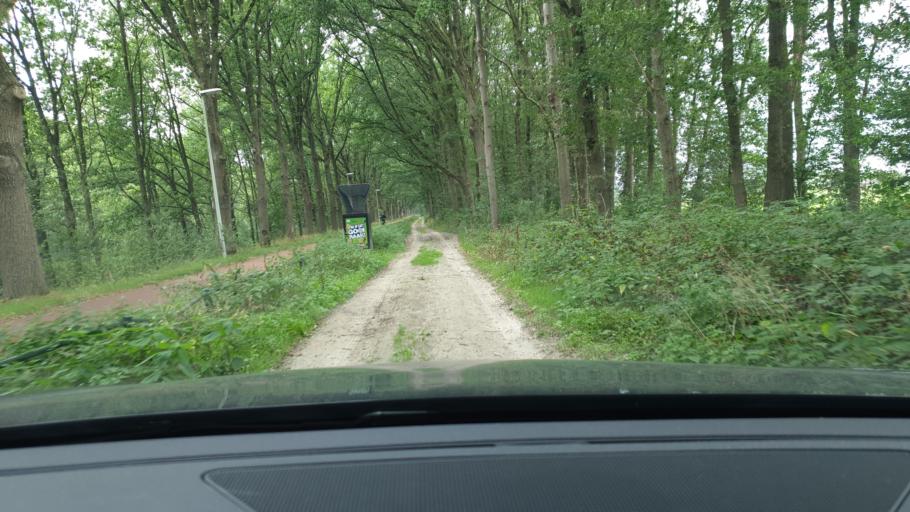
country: NL
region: North Brabant
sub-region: Gemeente Best
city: Best
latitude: 51.4971
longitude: 5.3568
